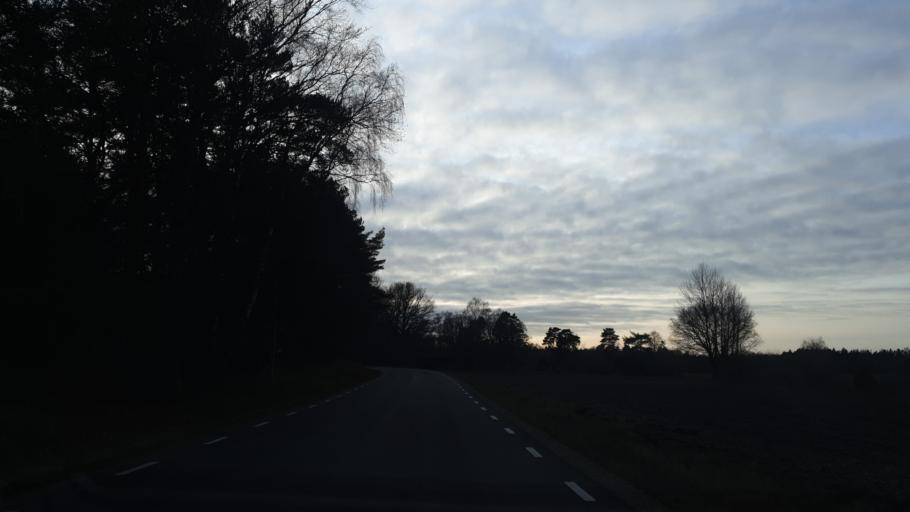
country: SE
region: Kalmar
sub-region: Torsas Kommun
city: Torsas
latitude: 56.2540
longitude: 16.0096
